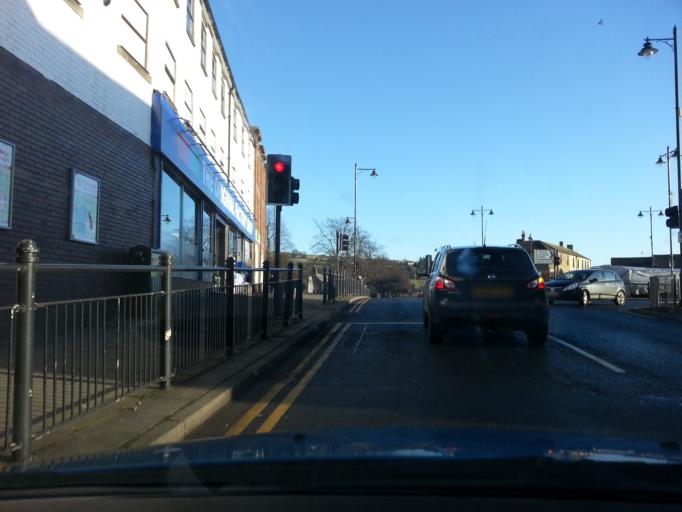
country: GB
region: England
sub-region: County Durham
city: Crook
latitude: 54.7147
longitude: -1.7469
